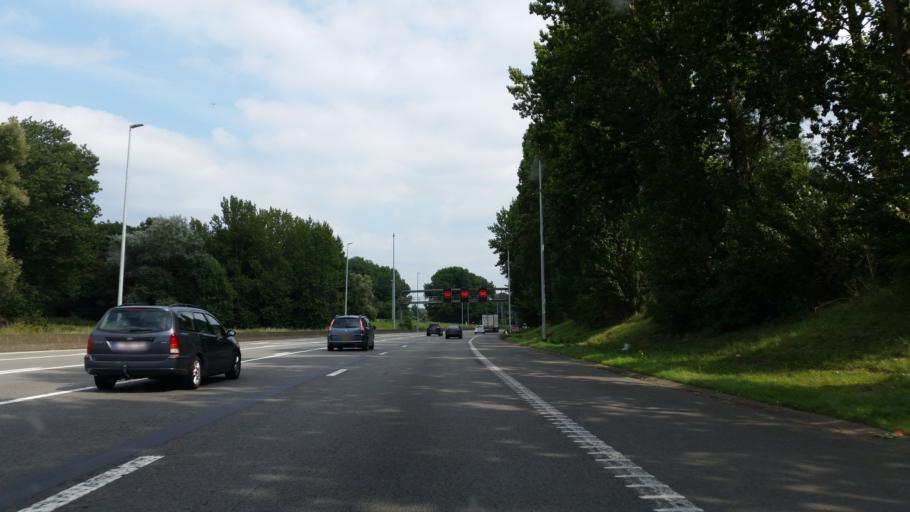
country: BE
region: Flanders
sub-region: Provincie Antwerpen
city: Zwijndrecht
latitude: 51.2136
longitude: 4.3583
